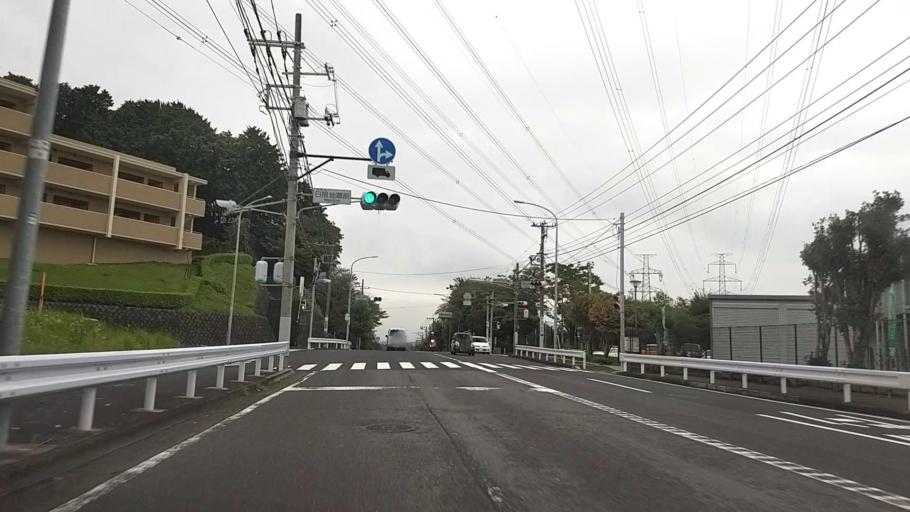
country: JP
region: Kanagawa
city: Kamakura
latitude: 35.3984
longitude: 139.5607
